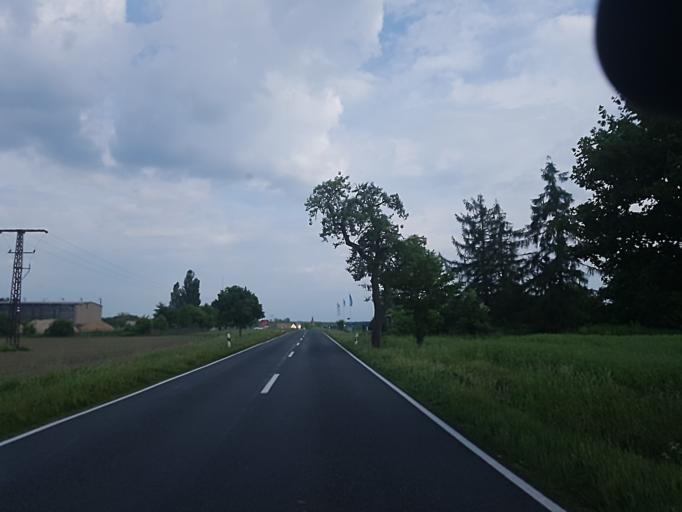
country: DE
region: Saxony-Anhalt
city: Klieken
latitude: 51.9193
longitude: 12.3979
